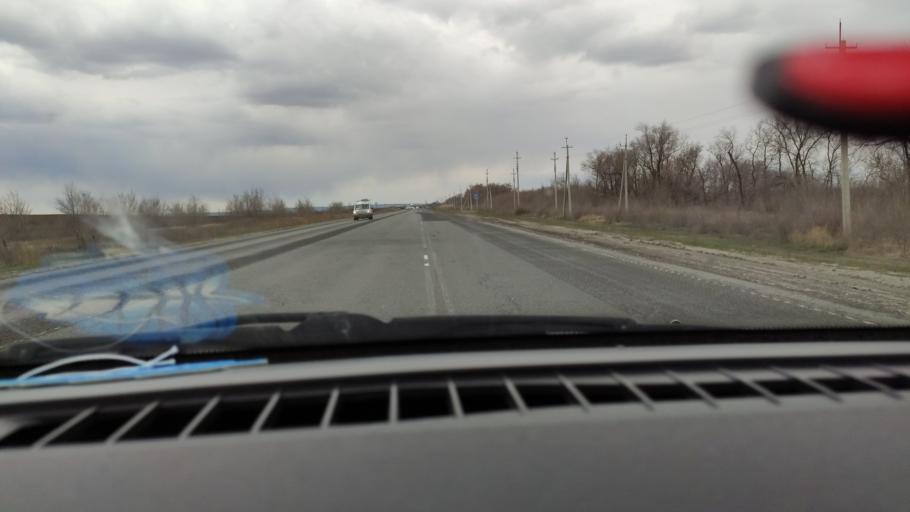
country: RU
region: Saratov
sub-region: Saratovskiy Rayon
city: Saratov
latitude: 51.7755
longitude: 46.0995
